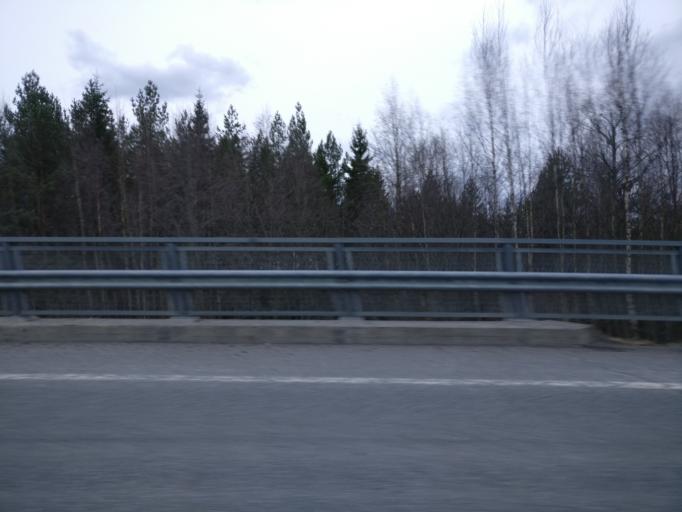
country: FI
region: Haeme
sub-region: Haemeenlinna
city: Parola
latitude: 61.0747
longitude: 24.2829
